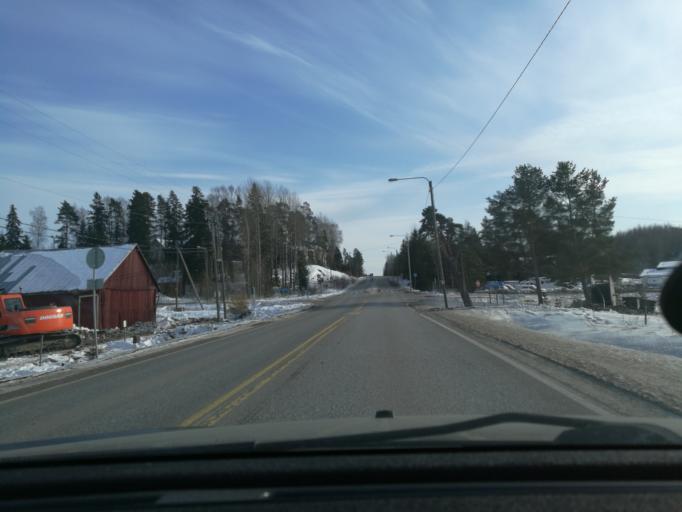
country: FI
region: Uusimaa
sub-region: Helsinki
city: Saukkola
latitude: 60.4011
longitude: 24.0648
